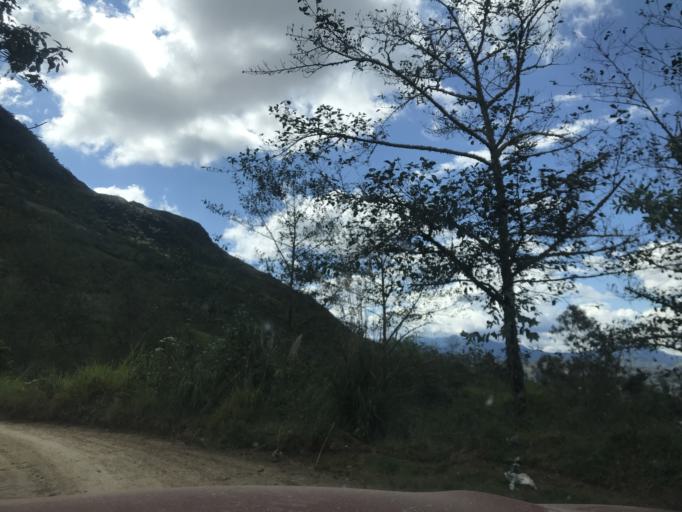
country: PE
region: Cajamarca
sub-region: Provincia de Chota
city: Querocoto
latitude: -6.3387
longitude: -79.0653
